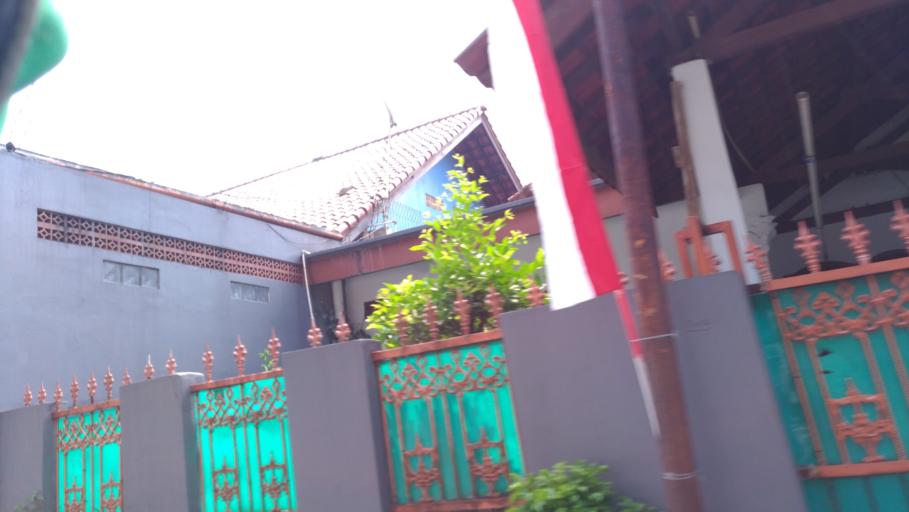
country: ID
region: West Java
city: Depok
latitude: -6.3520
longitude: 106.8671
